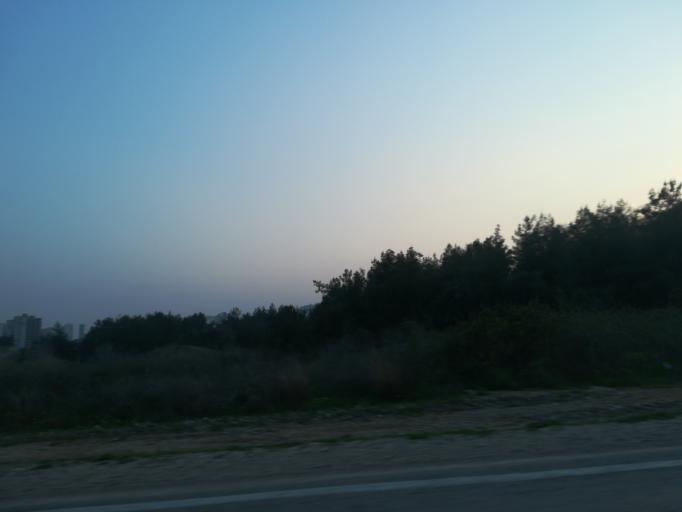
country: TR
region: Adana
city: Adana
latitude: 37.0739
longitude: 35.4048
